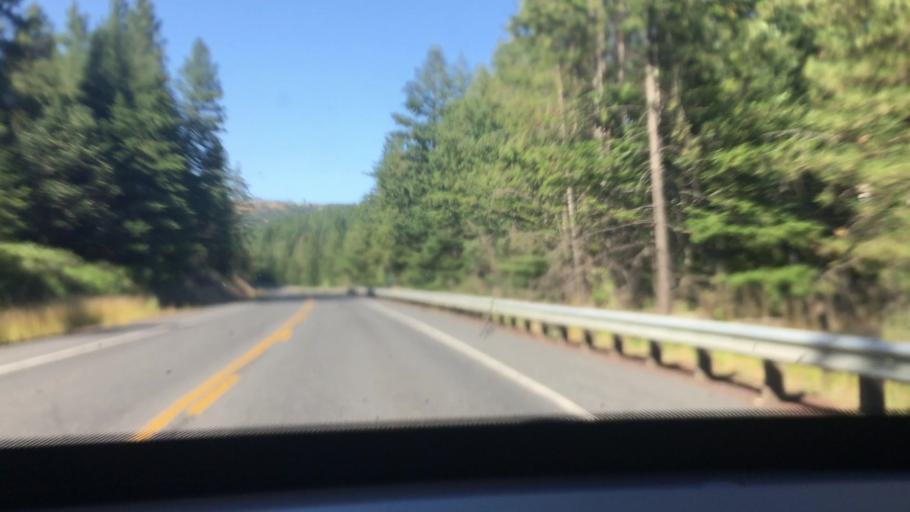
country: US
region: Washington
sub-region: Klickitat County
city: Goldendale
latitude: 45.9529
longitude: -120.6613
